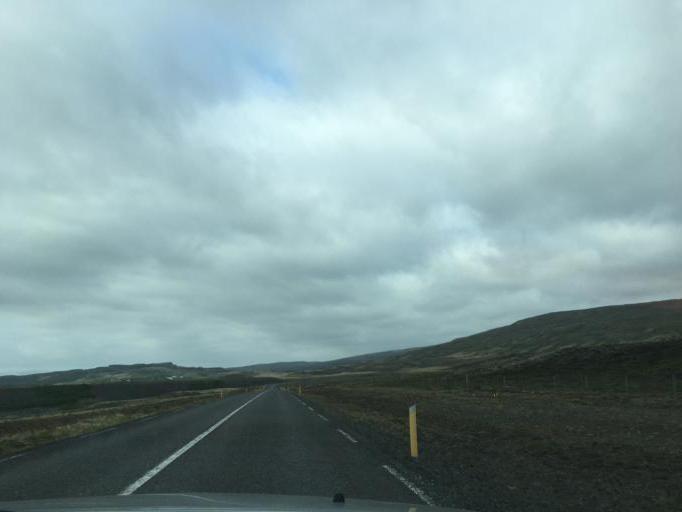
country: IS
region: South
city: Vestmannaeyjar
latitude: 64.2666
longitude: -20.2049
